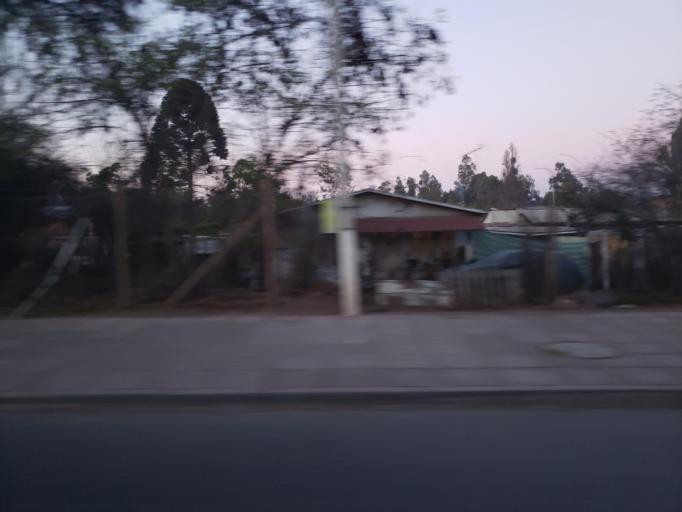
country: CL
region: Santiago Metropolitan
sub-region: Provincia de Talagante
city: El Monte
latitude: -33.6794
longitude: -70.9771
